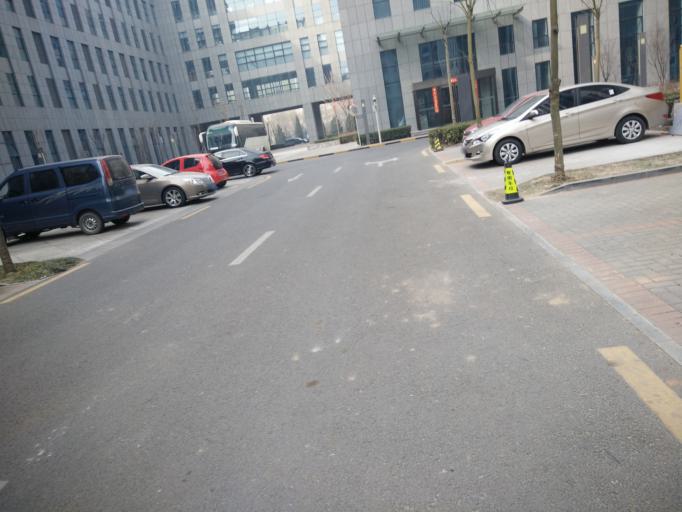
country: CN
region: Beijing
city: Jiugong
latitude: 39.7614
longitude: 116.5086
